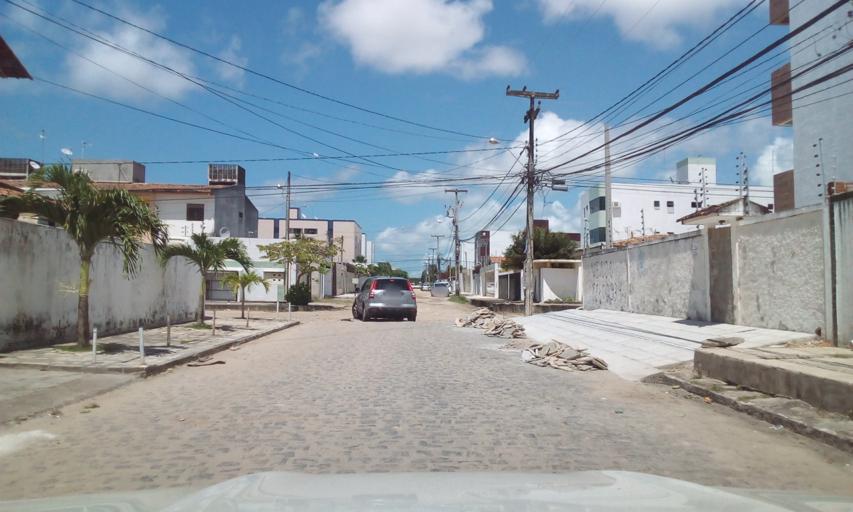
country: BR
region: Paraiba
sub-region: Joao Pessoa
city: Joao Pessoa
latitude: -7.1535
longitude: -34.8295
